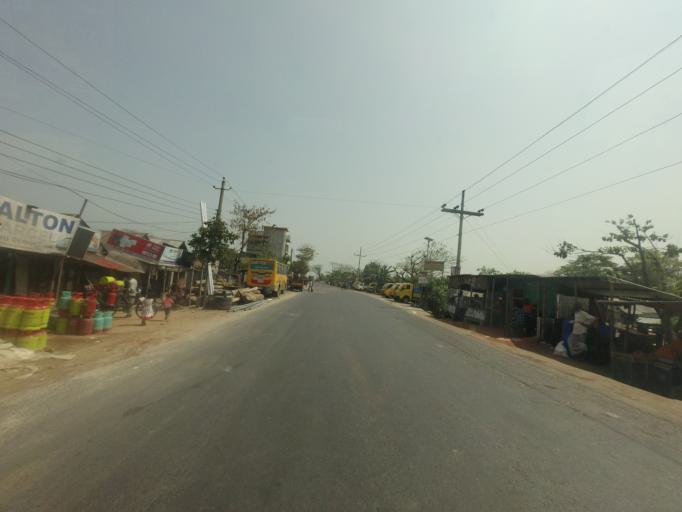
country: BD
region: Dhaka
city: Bhairab Bazar
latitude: 24.0543
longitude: 91.1481
